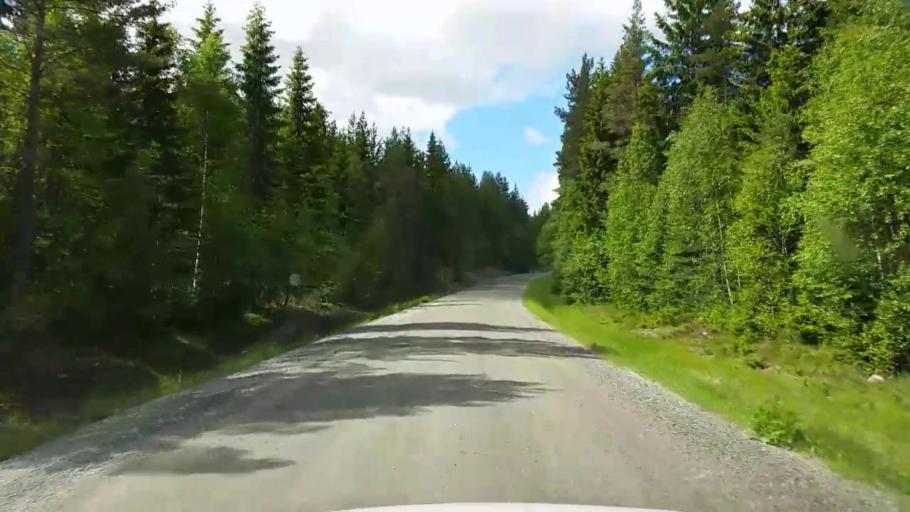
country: SE
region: Gaevleborg
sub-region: Bollnas Kommun
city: Vittsjo
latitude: 61.0923
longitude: 16.1732
